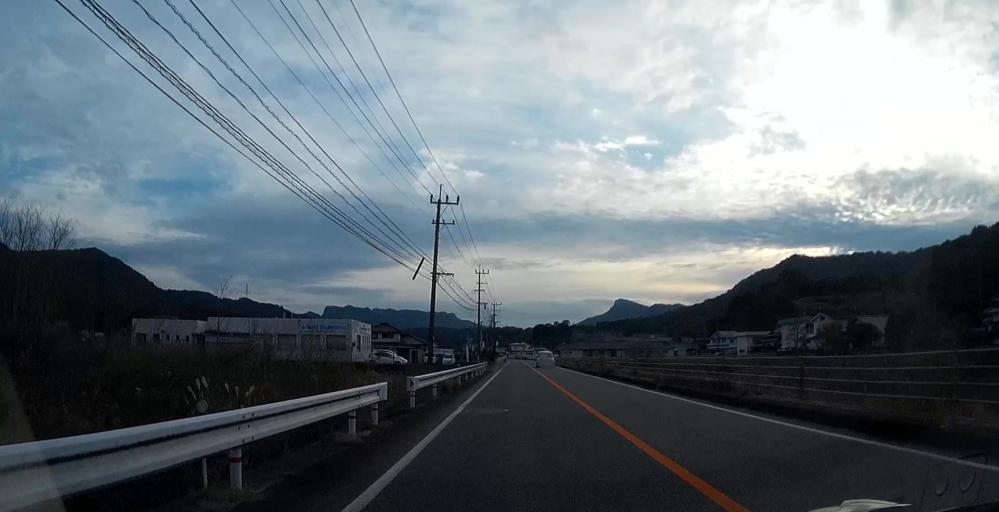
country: JP
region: Kumamoto
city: Yatsushiro
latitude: 32.5094
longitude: 130.4288
